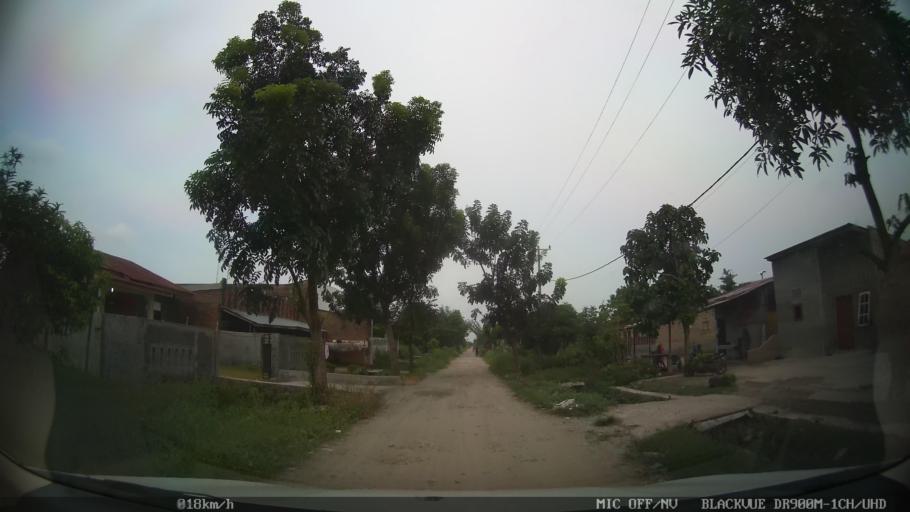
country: ID
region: North Sumatra
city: Medan
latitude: 3.5735
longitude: 98.7340
